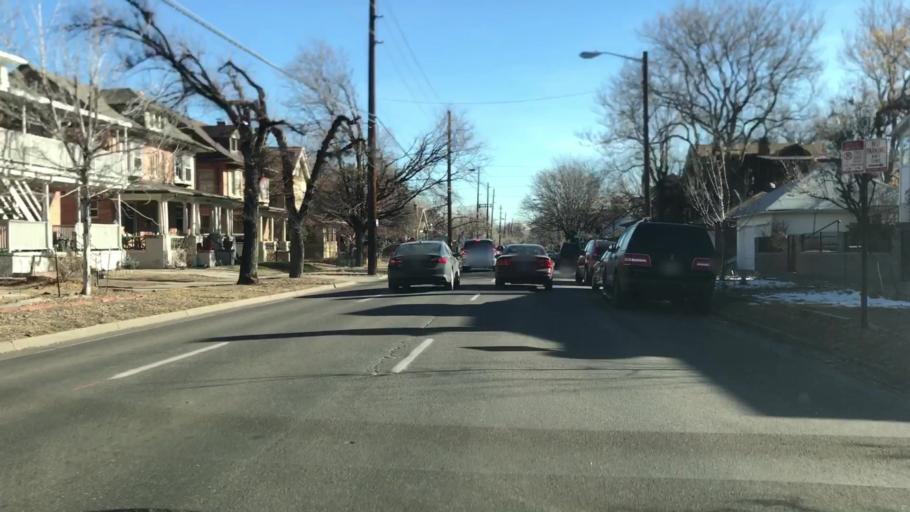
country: US
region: Colorado
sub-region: Arapahoe County
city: Glendale
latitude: 39.7384
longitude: -104.9472
